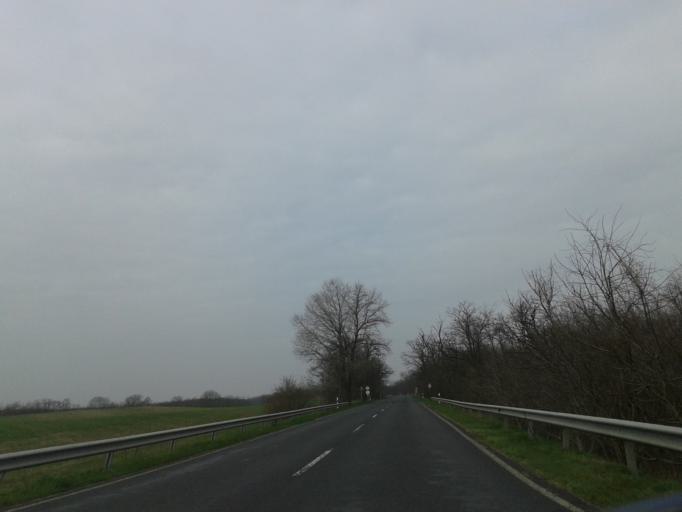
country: HU
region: Komarom-Esztergom
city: Acs
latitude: 47.7372
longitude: 17.9675
